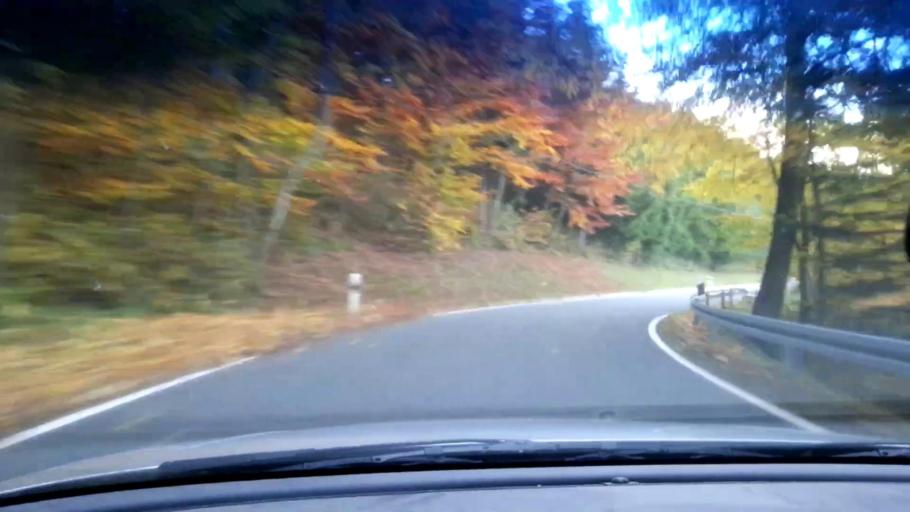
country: DE
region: Bavaria
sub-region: Upper Franconia
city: Heiligenstadt
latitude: 49.8607
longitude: 11.1226
